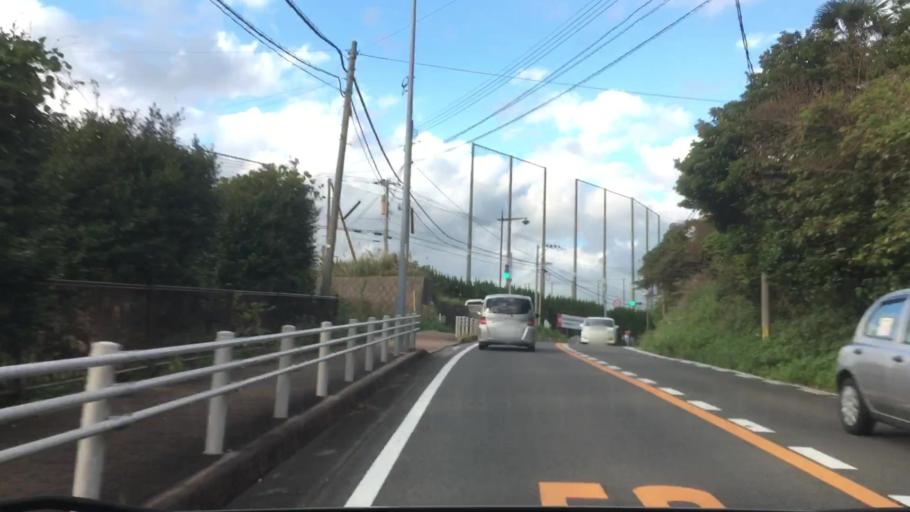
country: JP
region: Nagasaki
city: Togitsu
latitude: 32.9366
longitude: 129.6525
